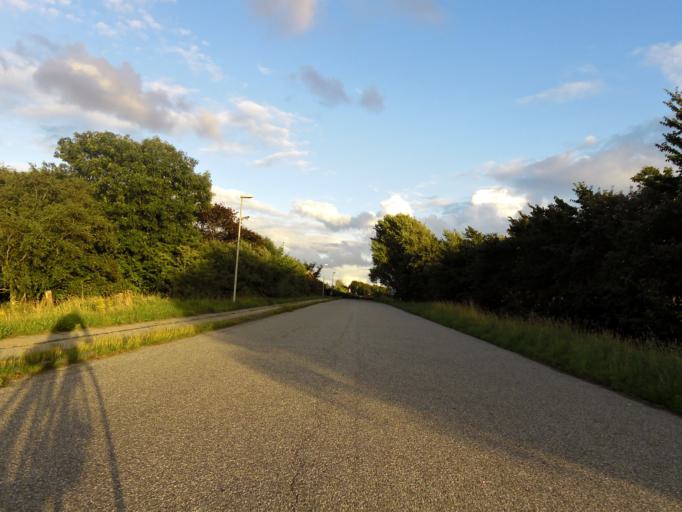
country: DK
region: South Denmark
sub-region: Esbjerg Kommune
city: Ribe
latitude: 55.3214
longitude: 8.7652
